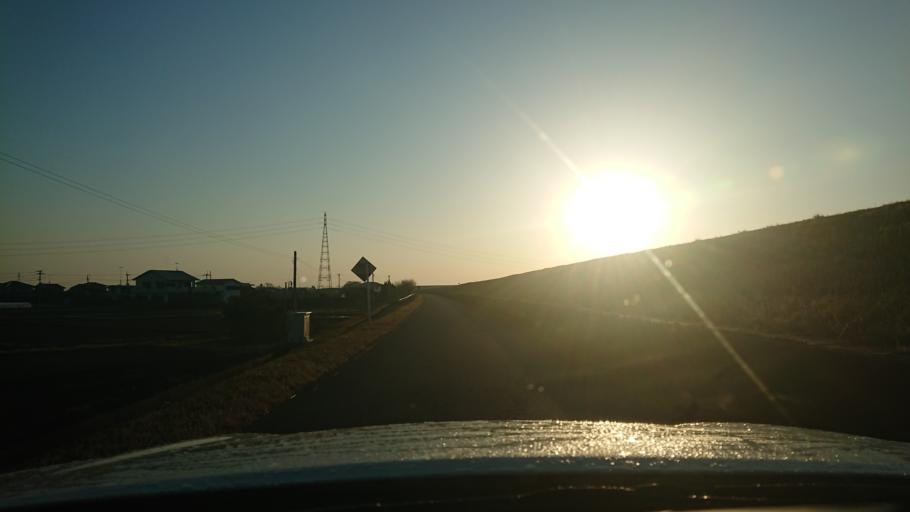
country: JP
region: Tokushima
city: Anan
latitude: 33.9410
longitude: 134.5993
